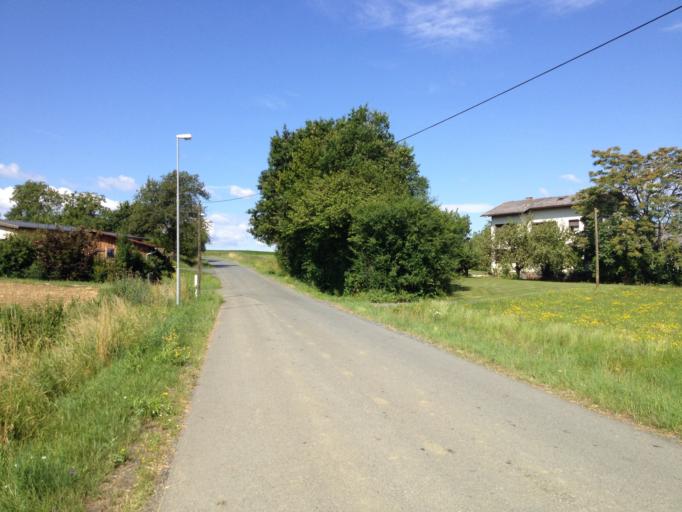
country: AT
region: Burgenland
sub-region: Politischer Bezirk Oberwart
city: Bad Tatzmannsdorf
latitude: 47.3224
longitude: 16.1942
